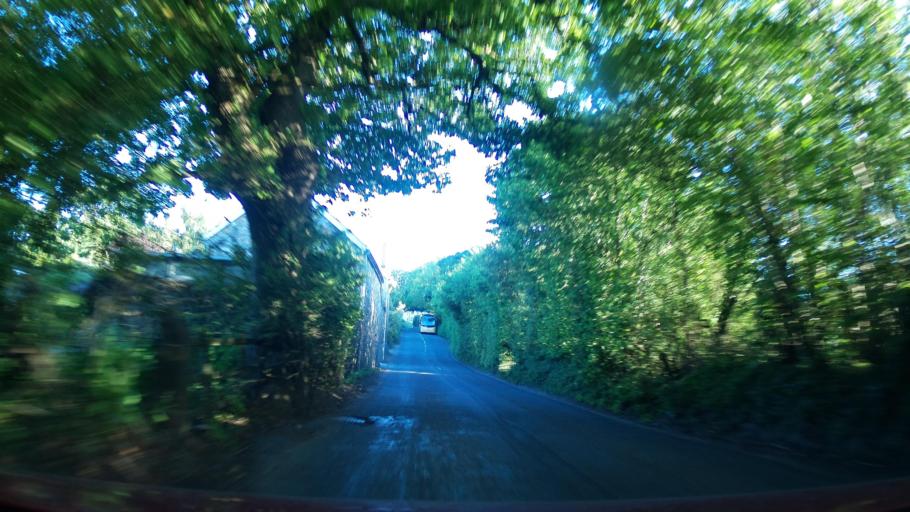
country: GB
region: England
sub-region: Devon
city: Newton Abbot
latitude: 50.5441
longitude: -3.6170
